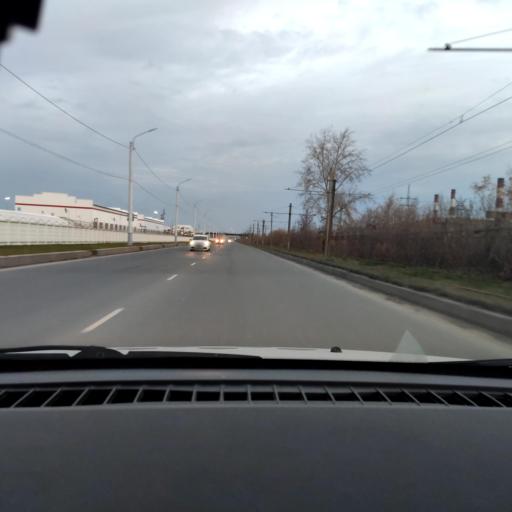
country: RU
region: Perm
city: Gamovo
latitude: 57.9167
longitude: 56.1511
